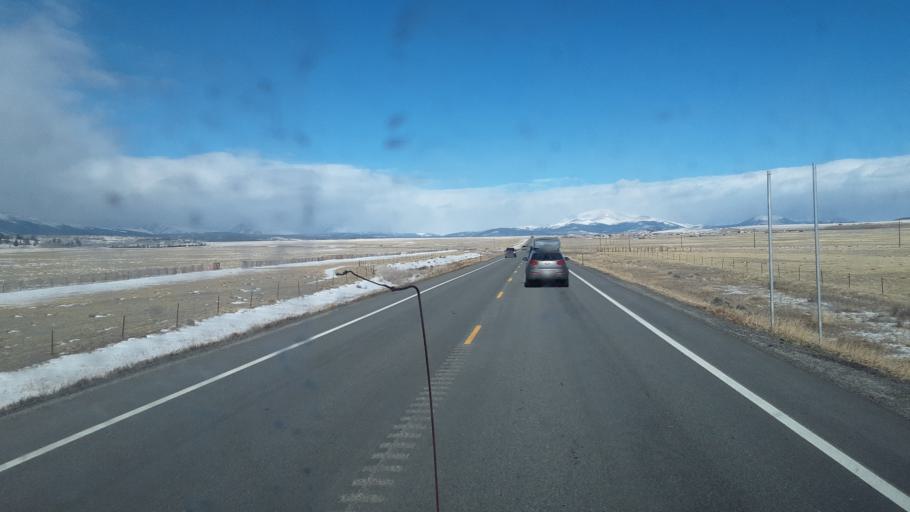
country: US
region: Colorado
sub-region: Park County
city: Fairplay
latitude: 39.1009
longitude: -105.9892
